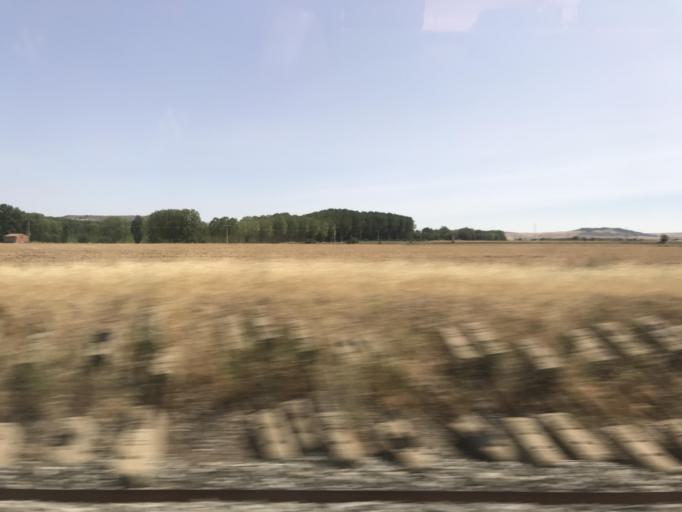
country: ES
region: Castille and Leon
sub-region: Provincia de Palencia
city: Palenzuela
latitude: 42.1033
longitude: -4.1700
